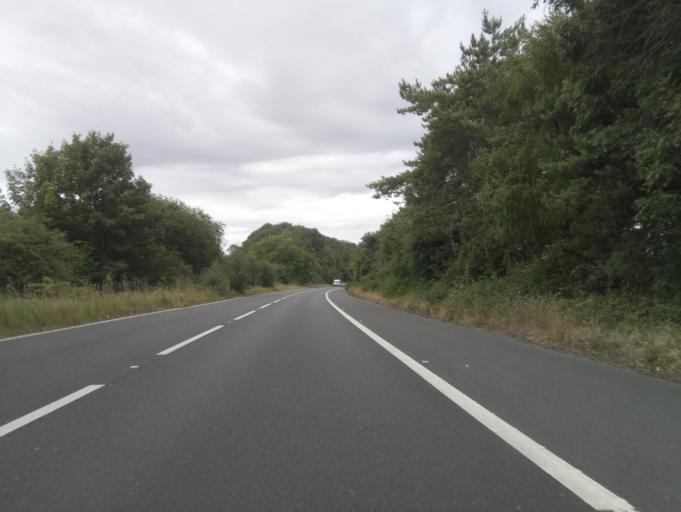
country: GB
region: England
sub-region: Hampshire
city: Overton
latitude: 51.2045
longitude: -1.1862
